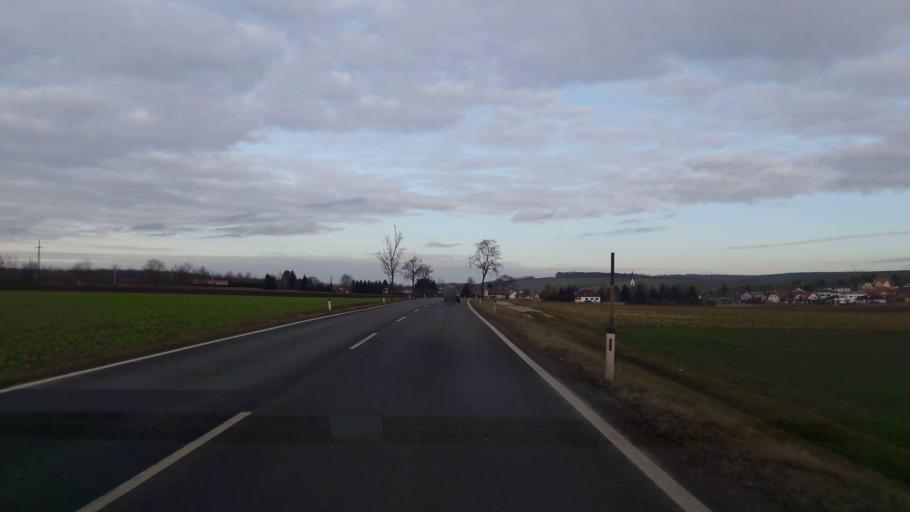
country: AT
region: Lower Austria
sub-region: Politischer Bezirk Mistelbach
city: Mistelbach
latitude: 48.5991
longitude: 16.5433
